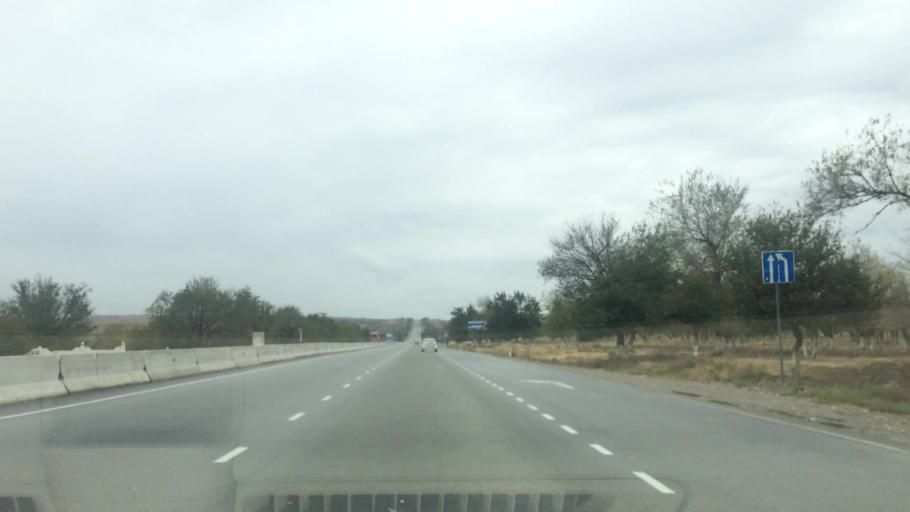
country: UZ
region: Samarqand
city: Bulung'ur
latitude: 39.8805
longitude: 67.4855
